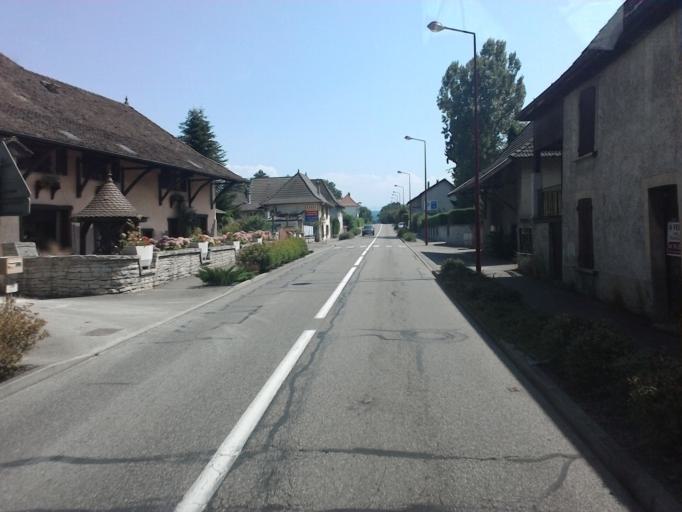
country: FR
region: Rhone-Alpes
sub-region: Departement de l'Isere
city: Les Abrets
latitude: 45.5483
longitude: 5.5766
